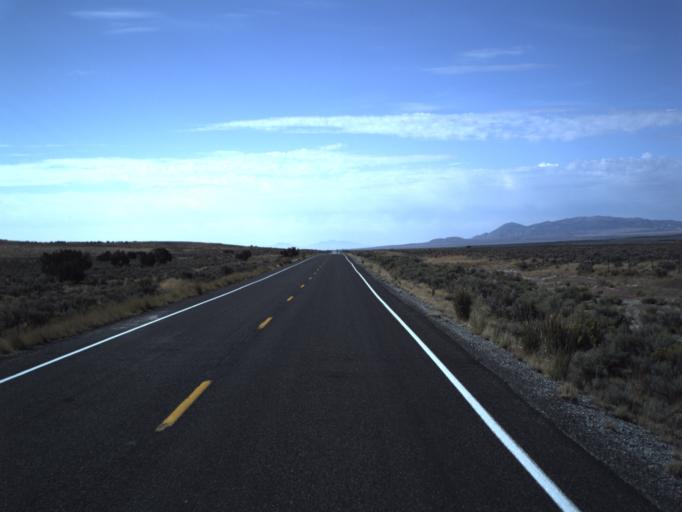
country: US
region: Idaho
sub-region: Cassia County
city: Burley
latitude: 41.6960
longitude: -113.5353
